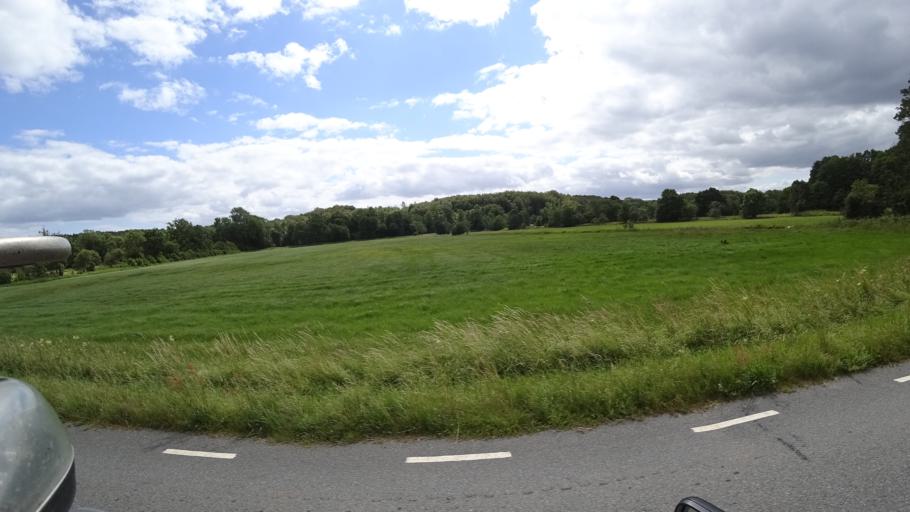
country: SE
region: Skane
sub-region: Kristianstads Kommun
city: Degeberga
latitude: 55.7280
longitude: 14.0705
